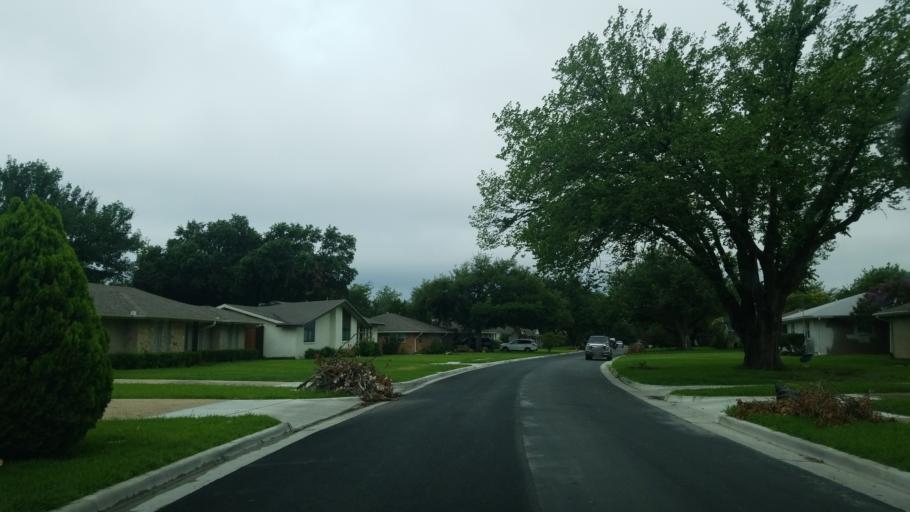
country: US
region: Texas
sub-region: Dallas County
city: Farmers Branch
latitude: 32.8998
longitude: -96.8665
